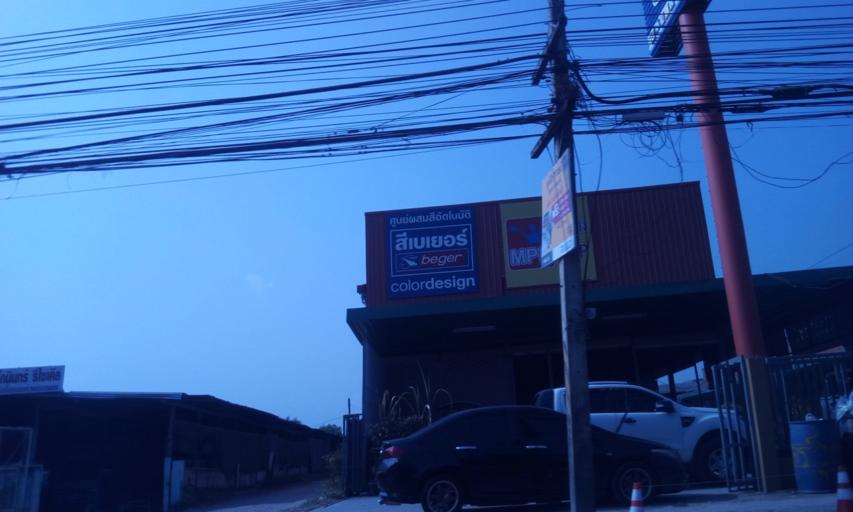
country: TH
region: Bangkok
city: Sai Mai
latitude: 13.9325
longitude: 100.6794
